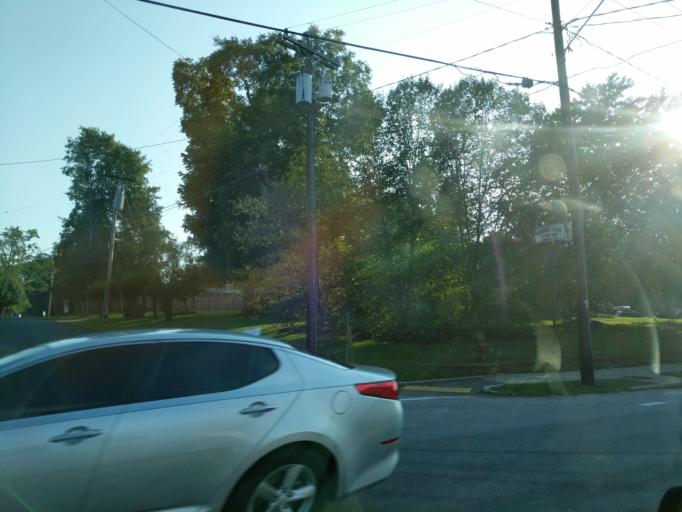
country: US
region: South Carolina
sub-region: Anderson County
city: Williamston
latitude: 34.6448
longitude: -82.4698
